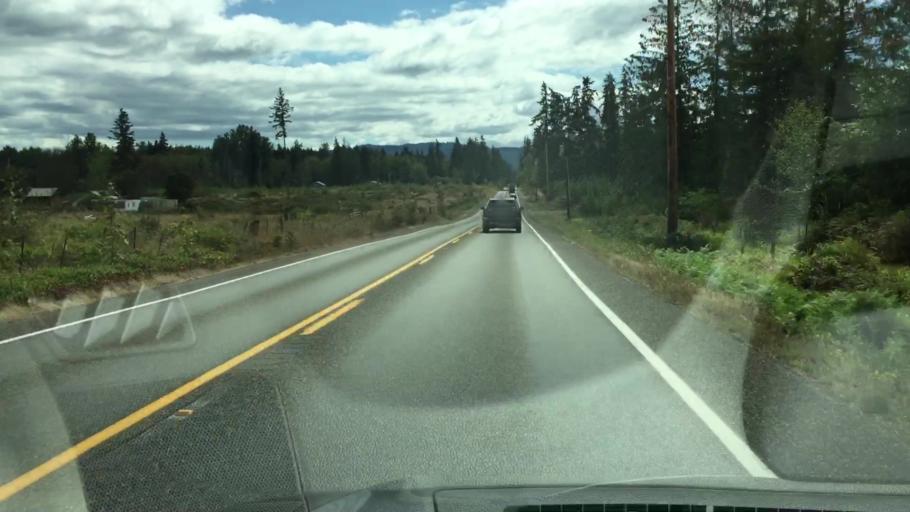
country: US
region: Washington
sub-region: Pierce County
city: Eatonville
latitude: 46.9052
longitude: -122.2979
